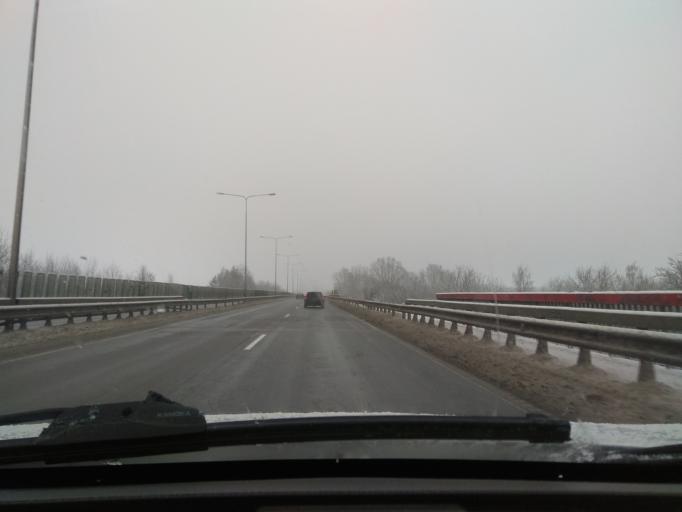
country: LT
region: Kauno apskritis
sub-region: Kauno rajonas
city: Karmelava
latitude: 54.9227
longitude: 24.0782
